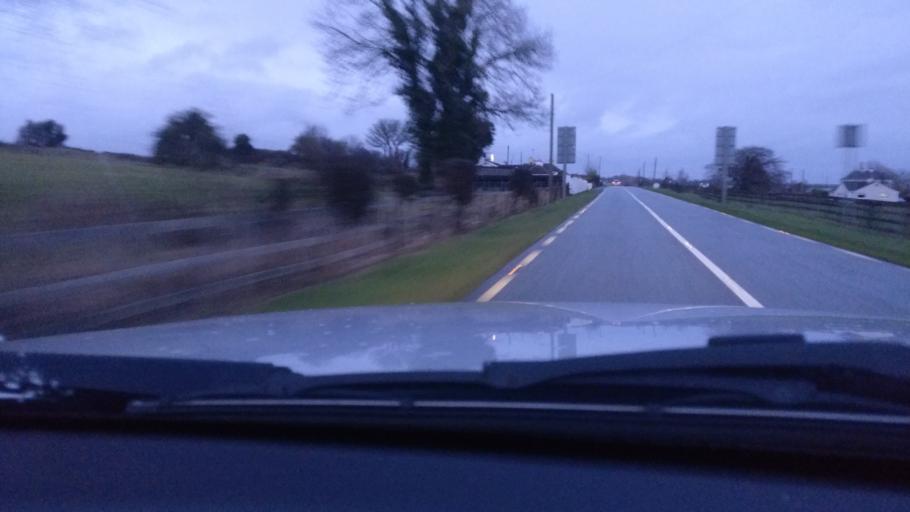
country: IE
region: Leinster
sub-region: An Iarmhi
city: Athlone
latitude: 53.4790
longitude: -7.8611
